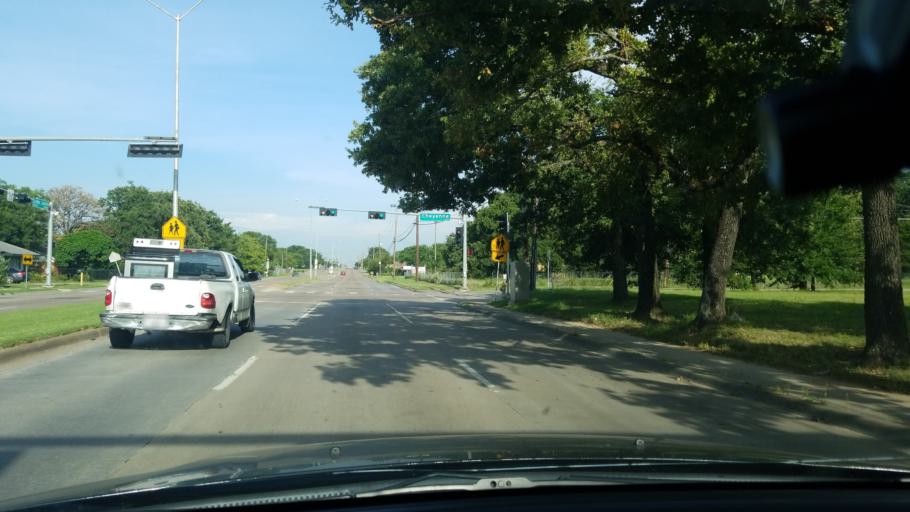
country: US
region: Texas
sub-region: Dallas County
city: Balch Springs
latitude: 32.7342
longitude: -96.6393
